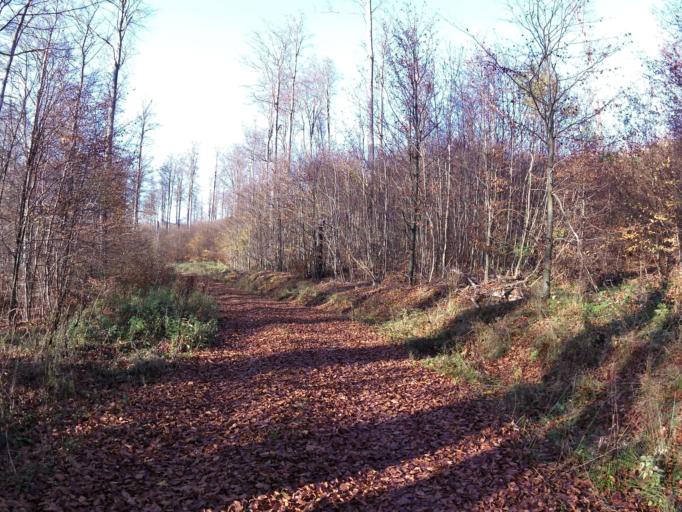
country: DE
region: Thuringia
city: Ruhla
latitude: 50.8766
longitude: 10.3946
